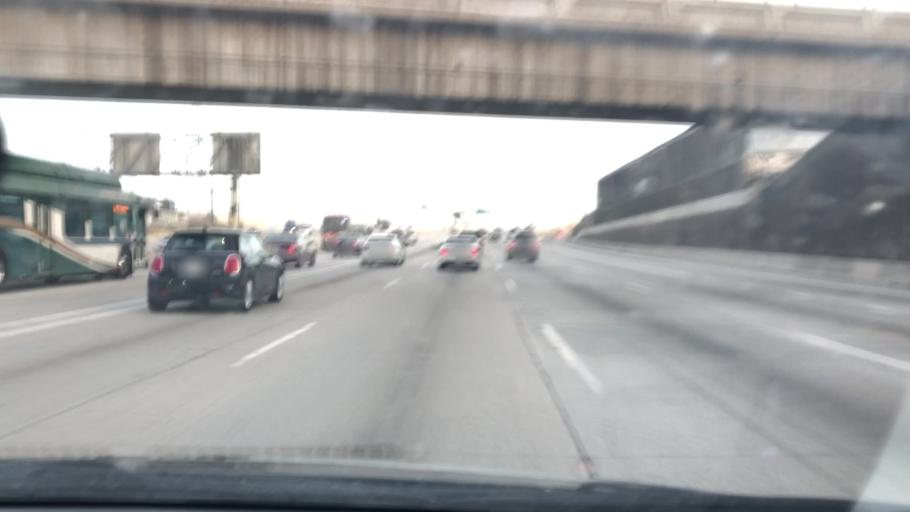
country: US
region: California
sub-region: Los Angeles County
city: West Rancho Dominguez
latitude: 33.8963
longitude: -118.2865
